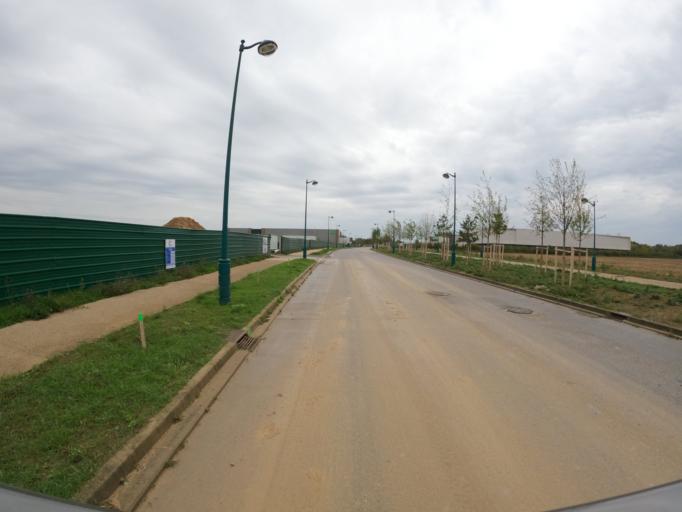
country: FR
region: Ile-de-France
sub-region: Departement de Seine-et-Marne
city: Serris
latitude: 48.8361
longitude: 2.7984
